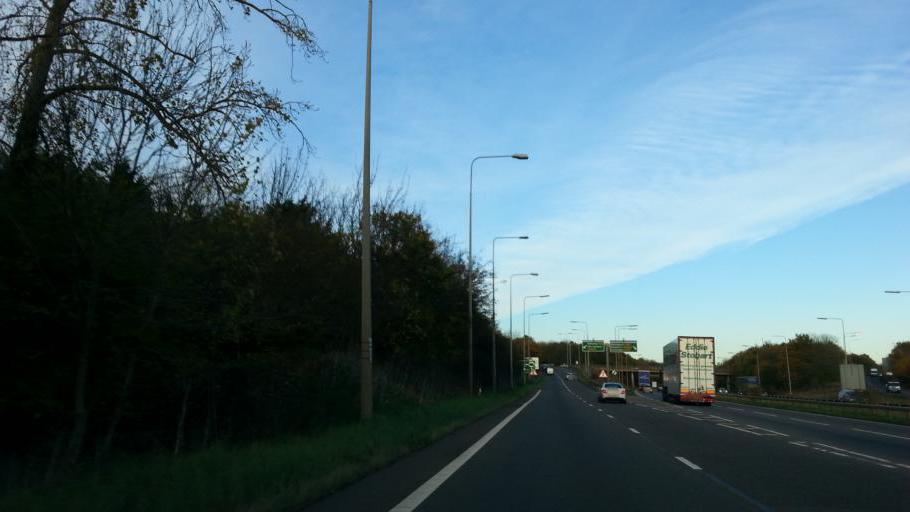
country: GB
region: England
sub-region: Northamptonshire
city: Northampton
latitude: 52.2430
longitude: -0.8409
